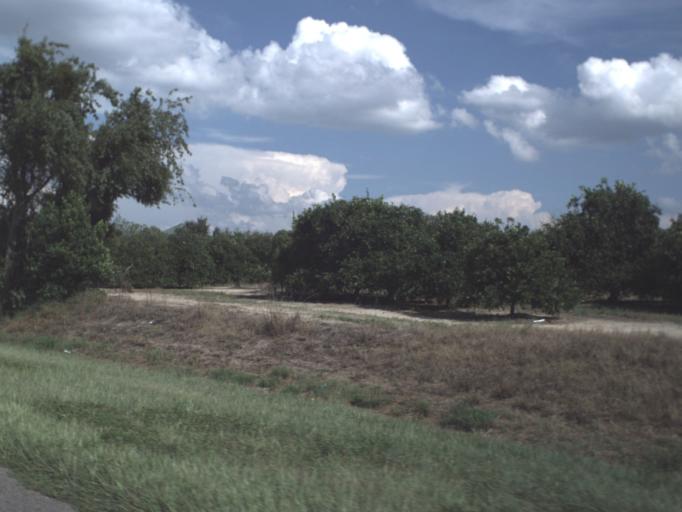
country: US
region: Florida
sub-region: Polk County
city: Lake Hamilton
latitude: 28.0808
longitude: -81.6378
